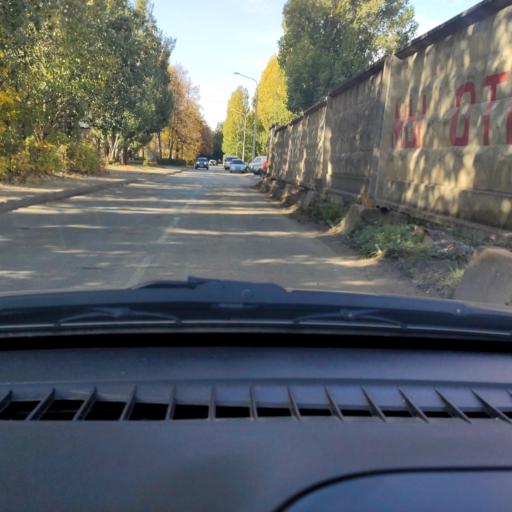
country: RU
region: Samara
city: Tol'yatti
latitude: 53.5327
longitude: 49.2924
